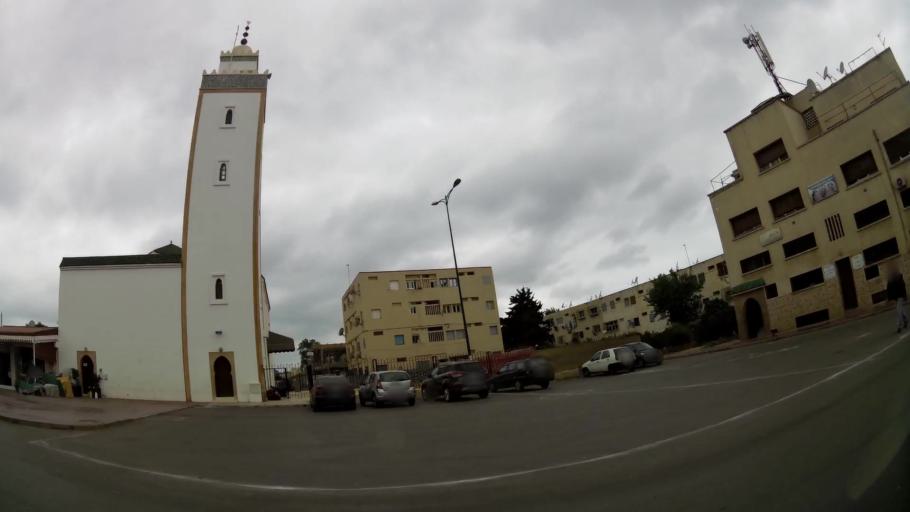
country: MA
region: Rabat-Sale-Zemmour-Zaer
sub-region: Rabat
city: Rabat
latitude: 33.9984
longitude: -6.8150
